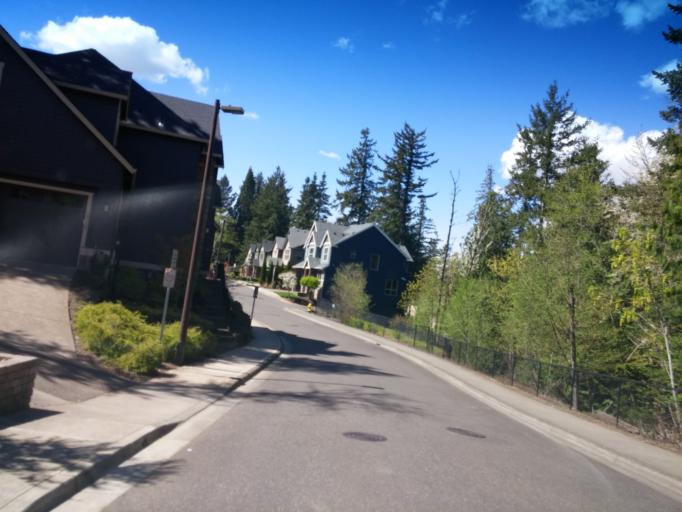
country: US
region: Oregon
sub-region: Washington County
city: West Haven
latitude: 45.5289
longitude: -122.7808
